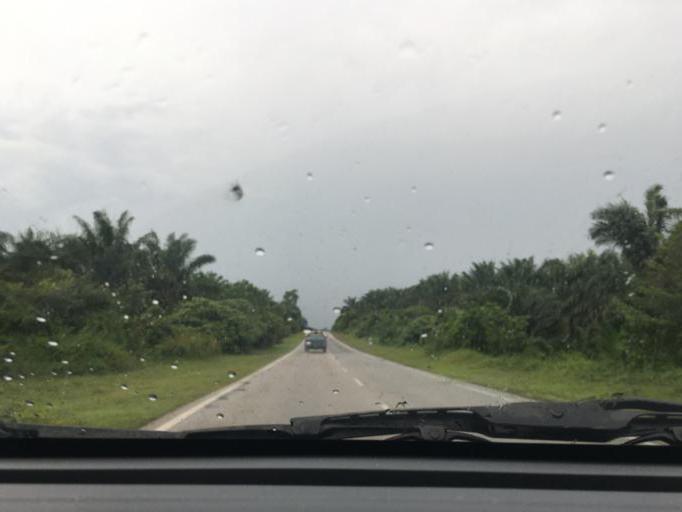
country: MY
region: Kedah
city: Sungai Petani
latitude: 5.6280
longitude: 100.6338
